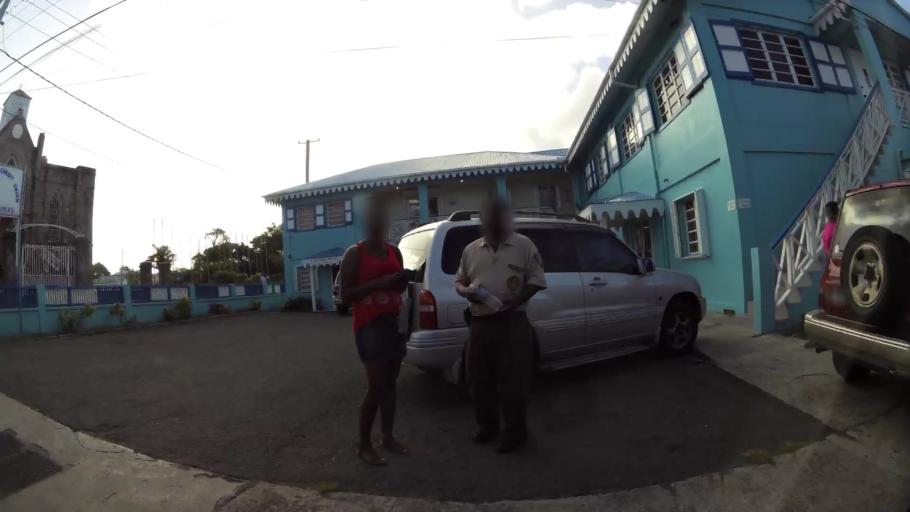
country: KN
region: Saint Paul Charlestown
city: Charlestown
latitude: 17.1400
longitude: -62.6282
